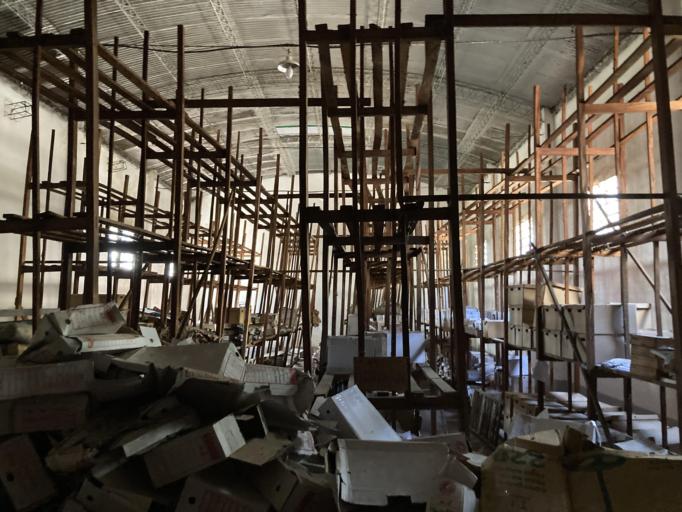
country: PY
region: Asuncion
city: Asuncion
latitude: -25.2792
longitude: -57.6155
